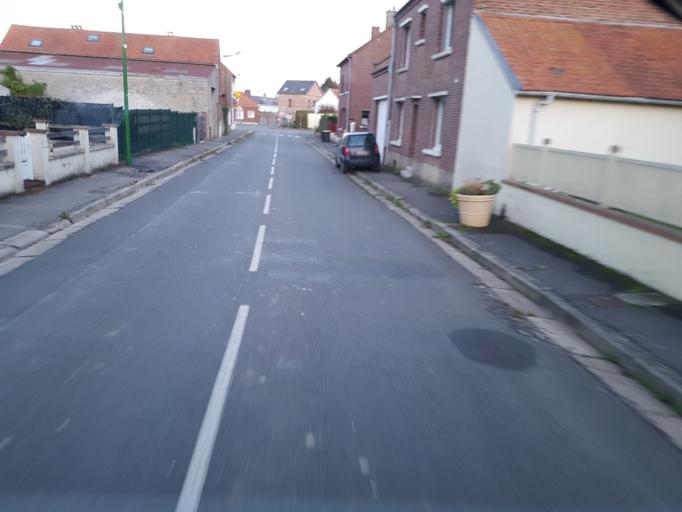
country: FR
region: Picardie
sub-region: Departement de la Somme
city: Sains-en-Amienois
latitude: 49.7680
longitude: 2.2693
